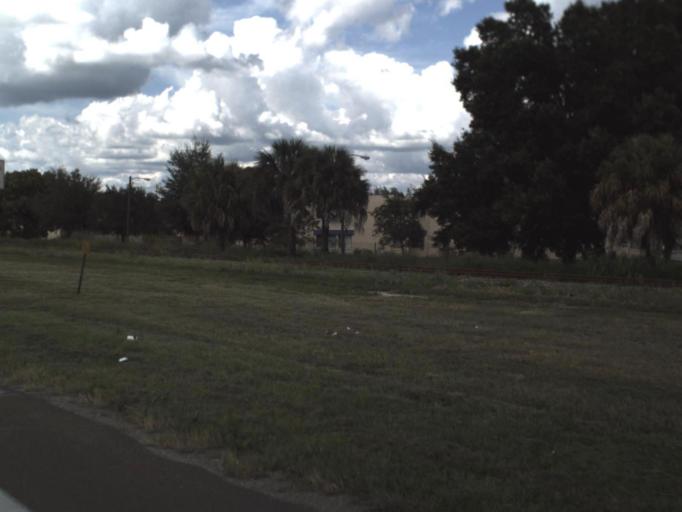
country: US
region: Florida
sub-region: Polk County
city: Lakeland
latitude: 28.0313
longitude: -81.9328
